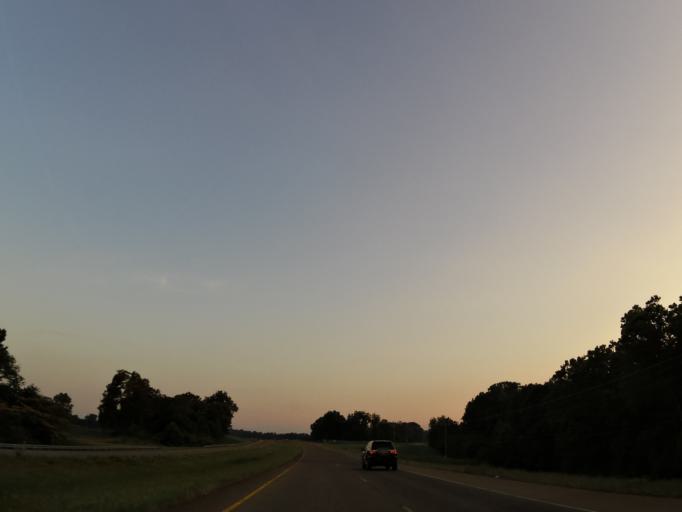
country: US
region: Tennessee
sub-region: Henry County
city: Paris
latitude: 36.2358
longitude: -88.3644
